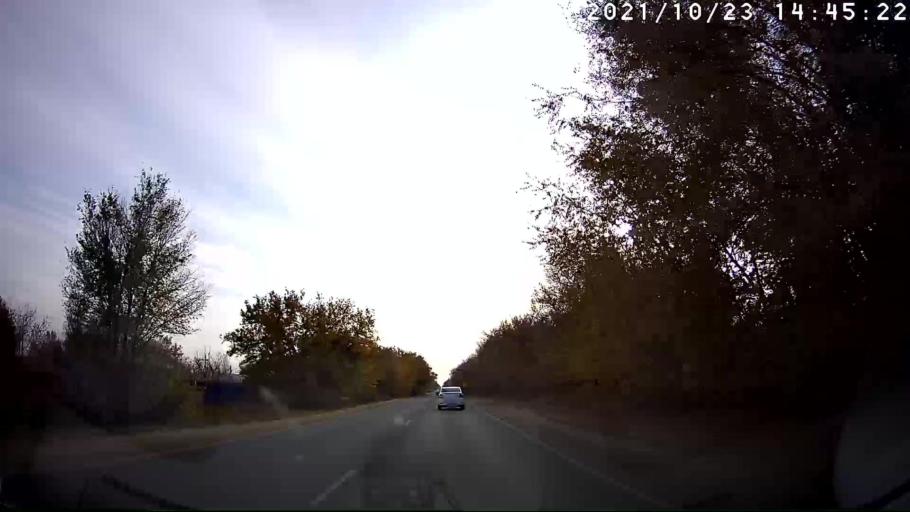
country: RU
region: Volgograd
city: Svetlyy Yar
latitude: 48.4452
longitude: 44.5133
